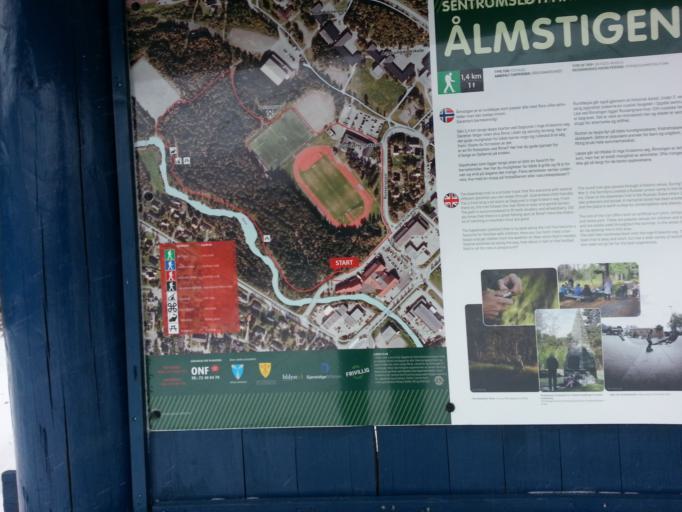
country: NO
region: Sor-Trondelag
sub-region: Oppdal
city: Oppdal
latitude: 62.5926
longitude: 9.6832
